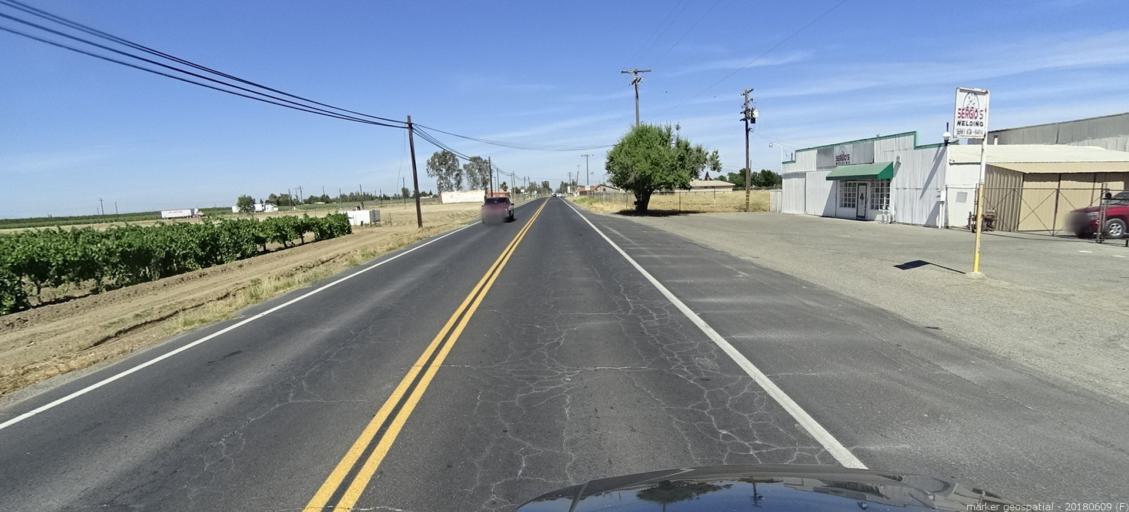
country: US
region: California
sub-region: Madera County
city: Madera
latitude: 36.9528
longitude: -120.0984
